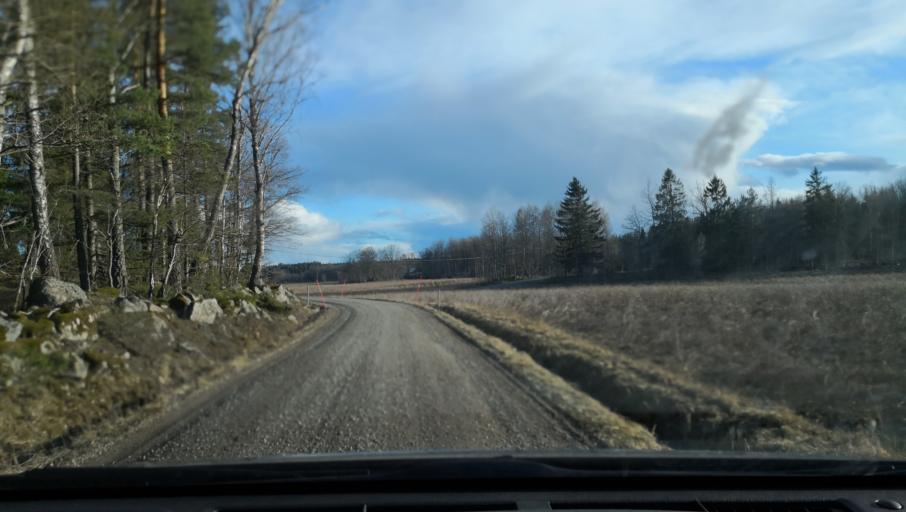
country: SE
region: Vaestmanland
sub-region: Arboga Kommun
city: Arboga
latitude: 59.4210
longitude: 15.7463
